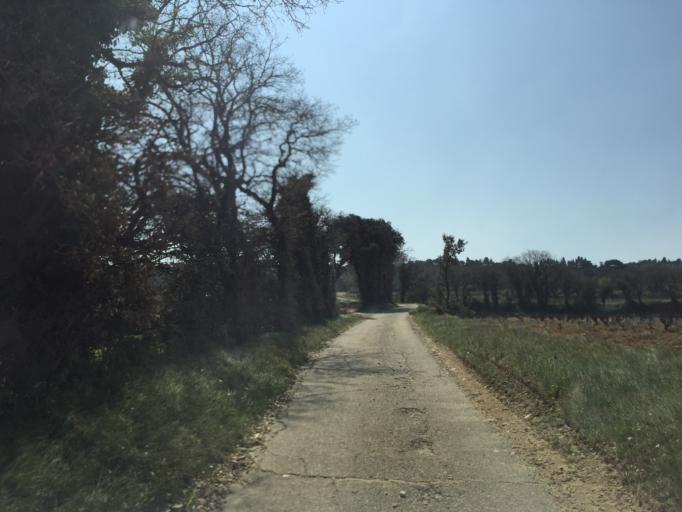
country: FR
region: Provence-Alpes-Cote d'Azur
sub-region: Departement du Vaucluse
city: Courthezon
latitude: 44.0647
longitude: 4.8731
